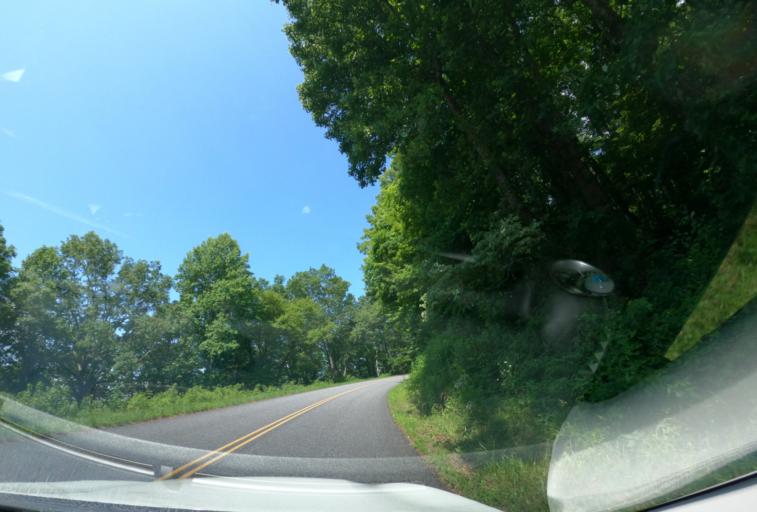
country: US
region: North Carolina
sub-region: Haywood County
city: Maggie Valley
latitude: 35.4397
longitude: -83.0856
